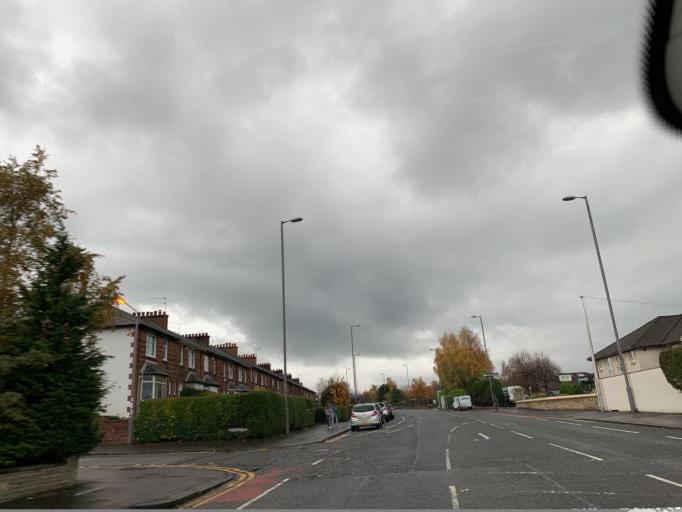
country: GB
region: Scotland
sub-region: East Renfrewshire
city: Giffnock
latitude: 55.8117
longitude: -4.2927
